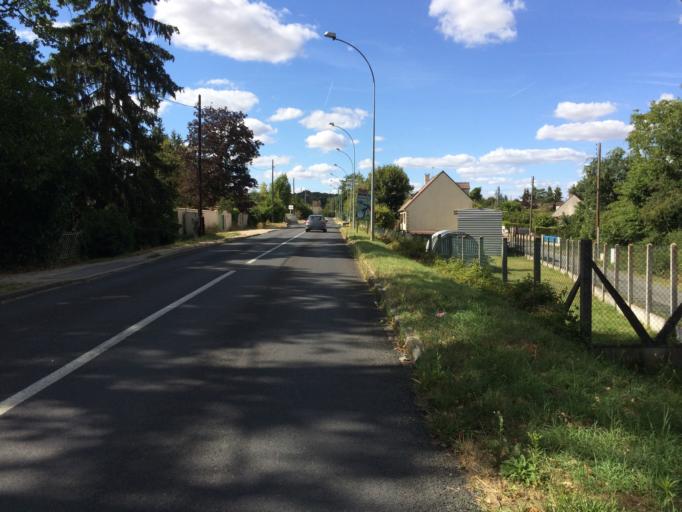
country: FR
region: Ile-de-France
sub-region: Departement de l'Essonne
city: Cerny
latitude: 48.4522
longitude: 2.3417
